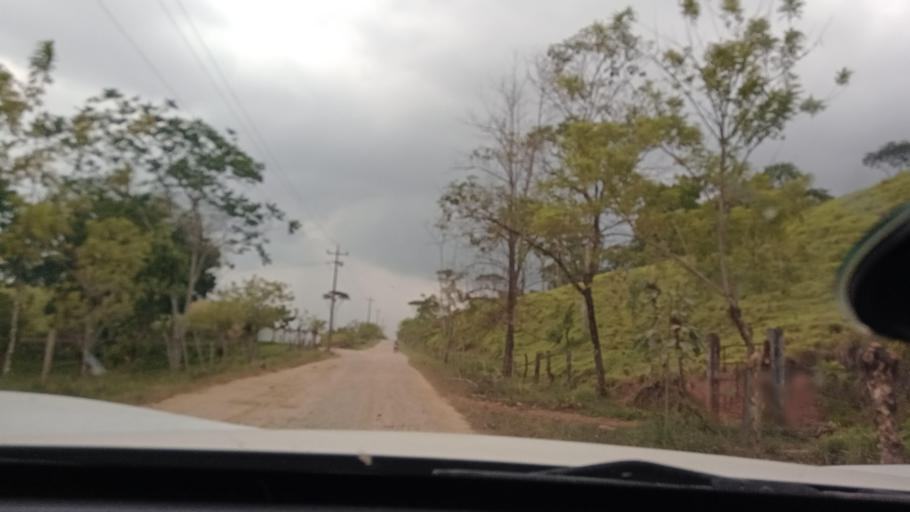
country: MX
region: Tabasco
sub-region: Huimanguillo
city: Francisco Rueda
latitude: 17.4342
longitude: -94.0505
